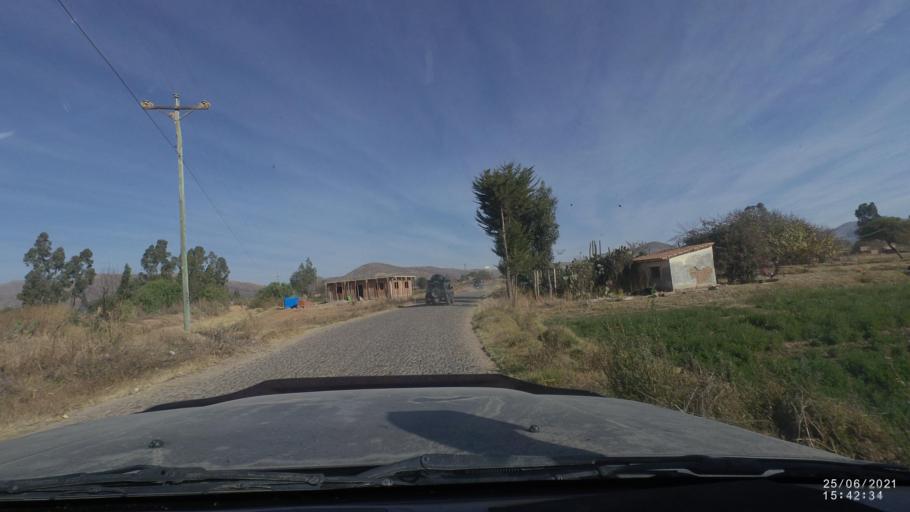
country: BO
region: Cochabamba
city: Cliza
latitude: -17.6403
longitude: -65.9114
